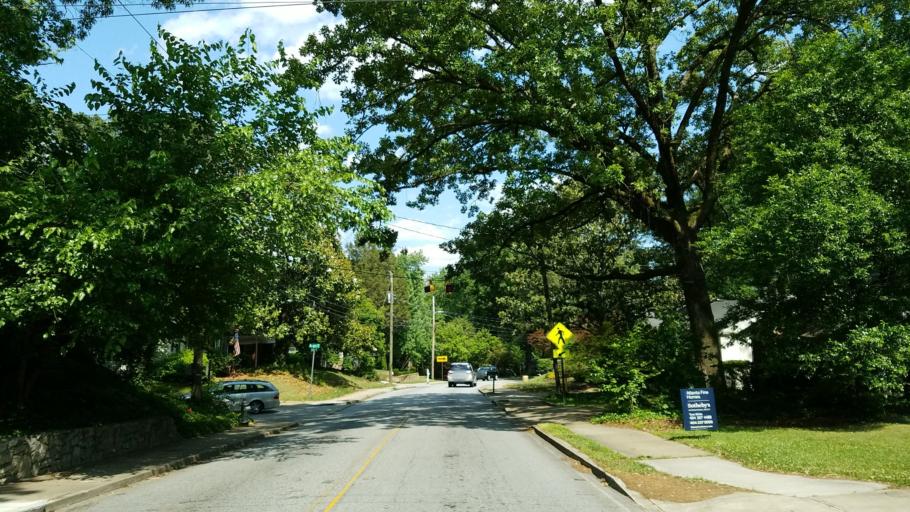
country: US
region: Georgia
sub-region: DeKalb County
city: North Atlanta
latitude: 33.8228
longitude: -84.3789
